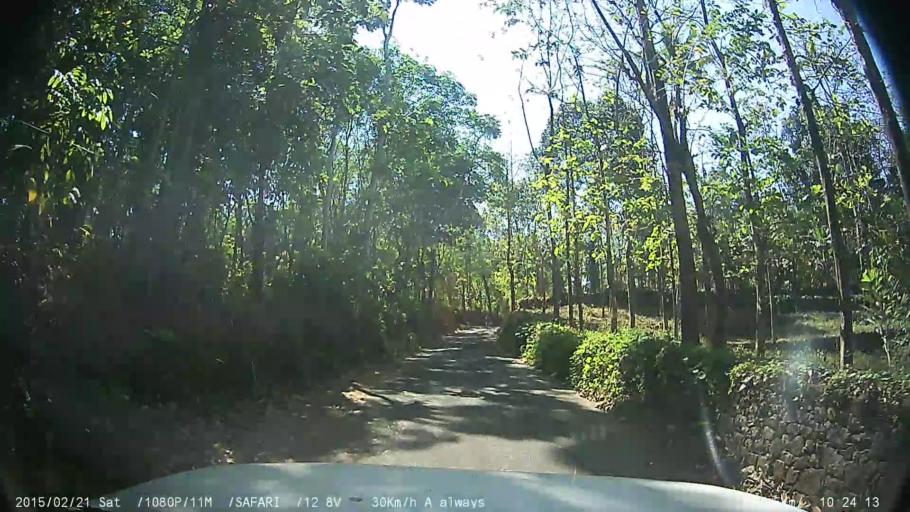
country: IN
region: Kerala
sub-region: Kottayam
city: Palackattumala
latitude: 9.8579
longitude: 76.6790
